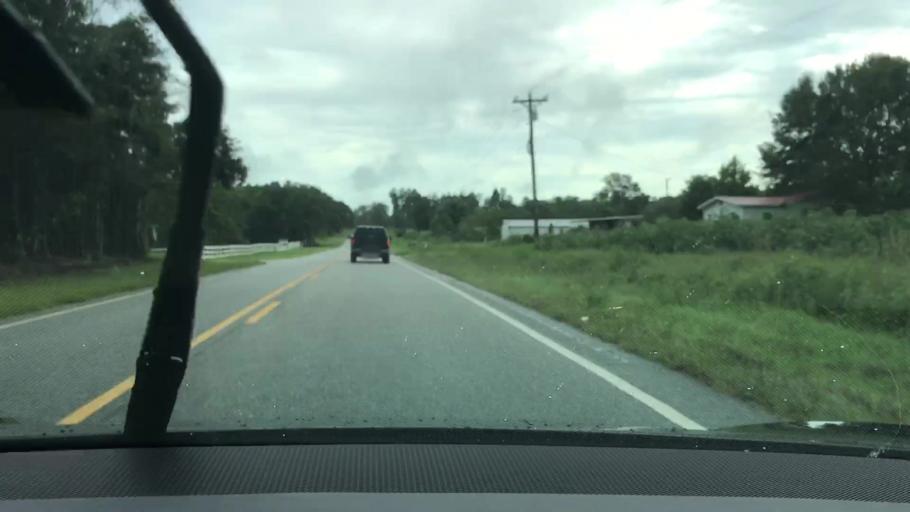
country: US
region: Alabama
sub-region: Geneva County
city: Samson
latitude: 31.1031
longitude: -86.1115
